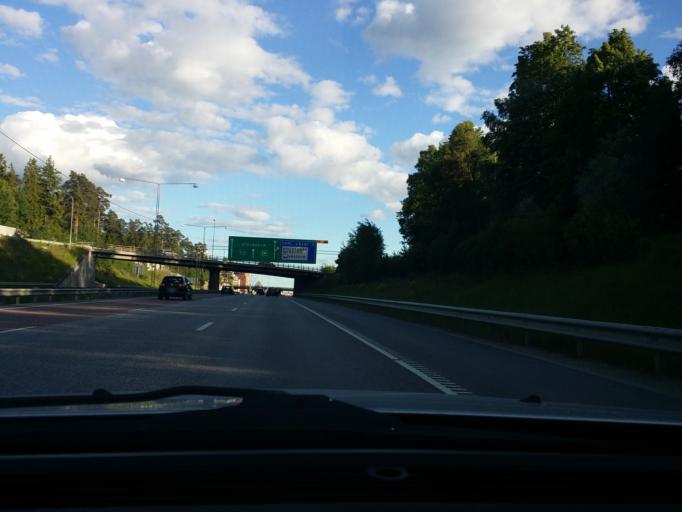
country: SE
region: Stockholm
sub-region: Upplands Vasby Kommun
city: Upplands Vaesby
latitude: 59.5068
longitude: 17.9243
